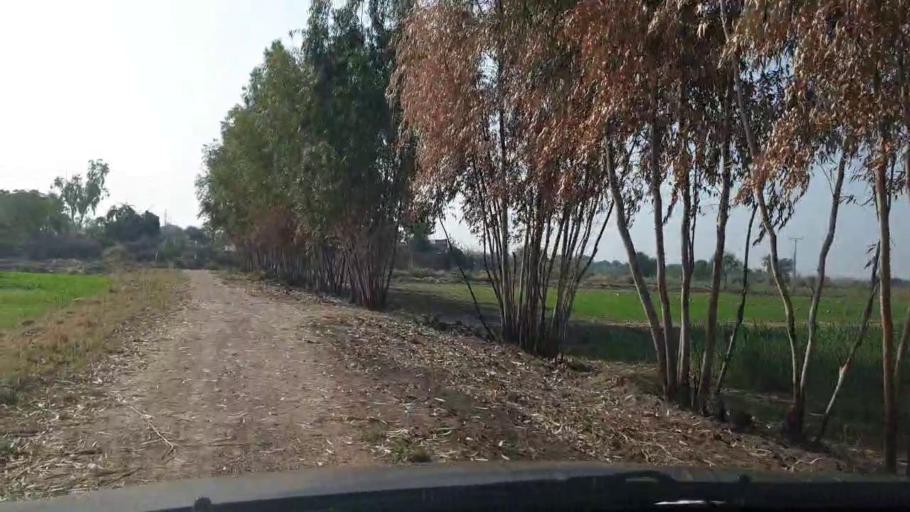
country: PK
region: Sindh
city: Jhol
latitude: 25.9646
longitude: 68.9455
